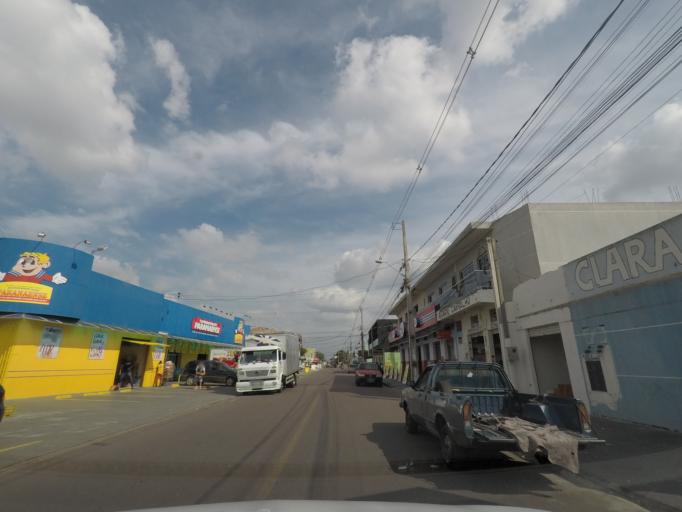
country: BR
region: Parana
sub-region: Sao Jose Dos Pinhais
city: Sao Jose dos Pinhais
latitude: -25.4888
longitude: -49.2000
